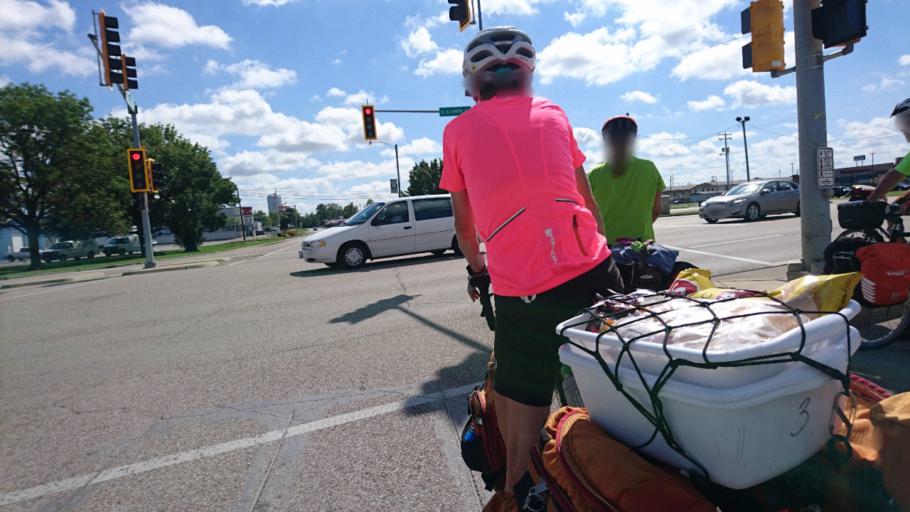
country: US
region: Illinois
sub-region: Montgomery County
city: Litchfield
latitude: 39.1783
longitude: -89.6665
